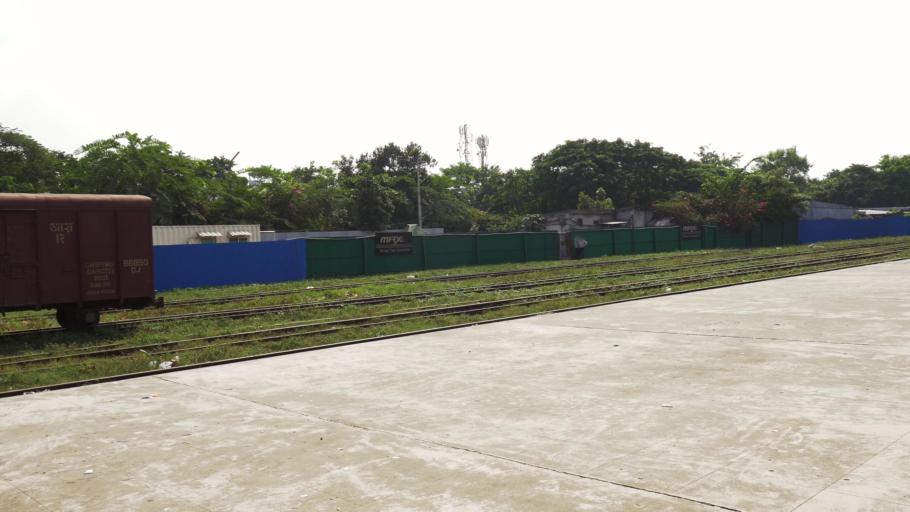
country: BD
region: Dhaka
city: Tungi
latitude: 23.8638
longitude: 90.4061
